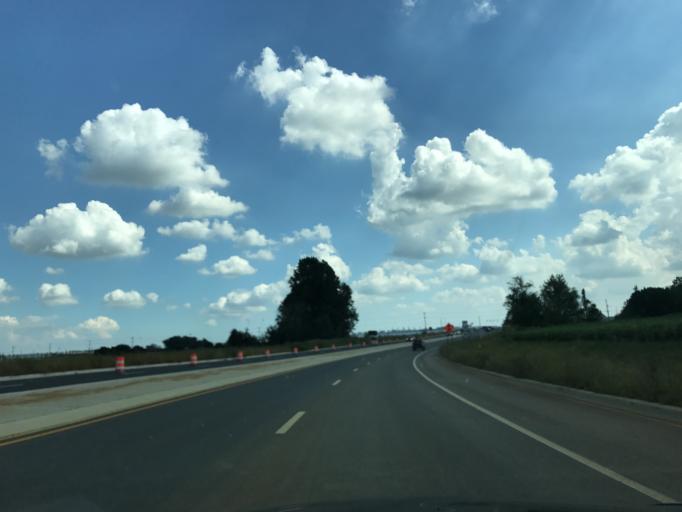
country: US
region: Delaware
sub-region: New Castle County
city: Middletown
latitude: 39.4435
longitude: -75.7497
